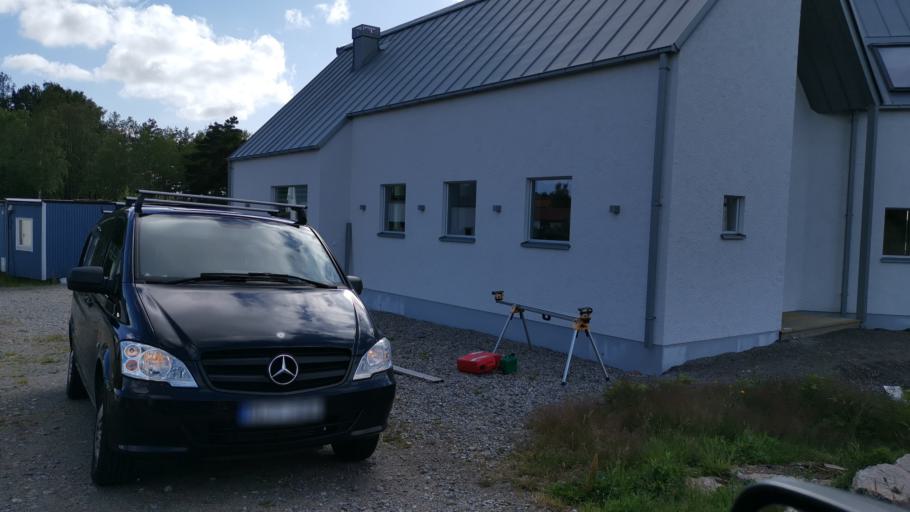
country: SE
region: Vaestra Goetaland
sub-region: Tjorns Kommun
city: Myggenas
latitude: 58.1041
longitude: 11.6387
